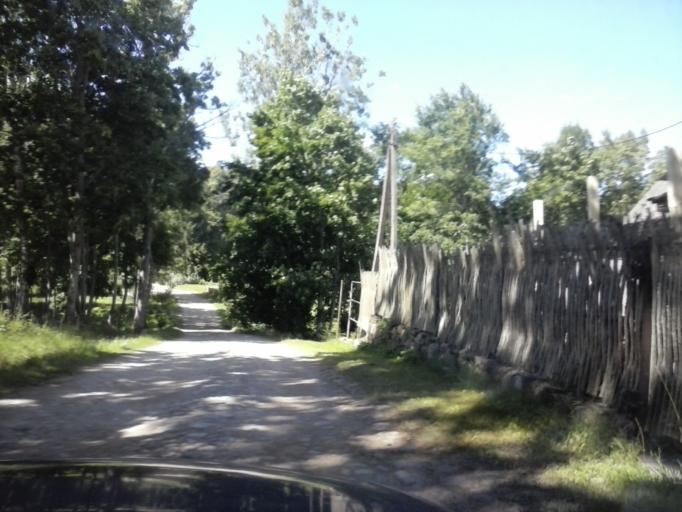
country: LV
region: Apes Novads
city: Ape
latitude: 57.5728
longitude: 26.6672
